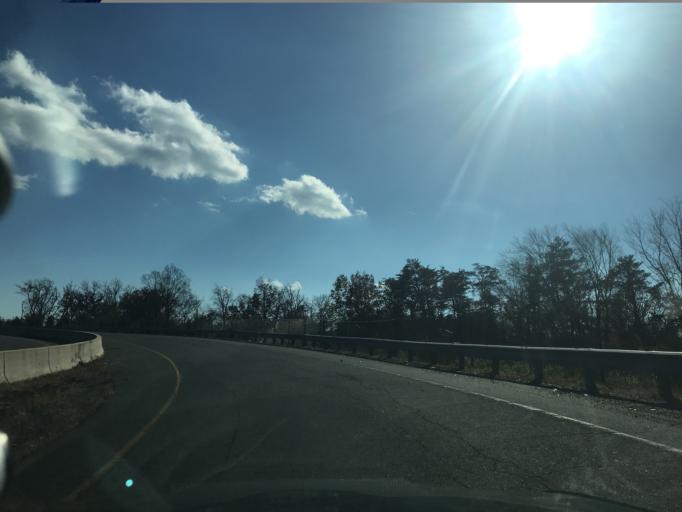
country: US
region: Virginia
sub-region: Fairfax County
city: Floris
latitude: 38.9495
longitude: -77.4313
